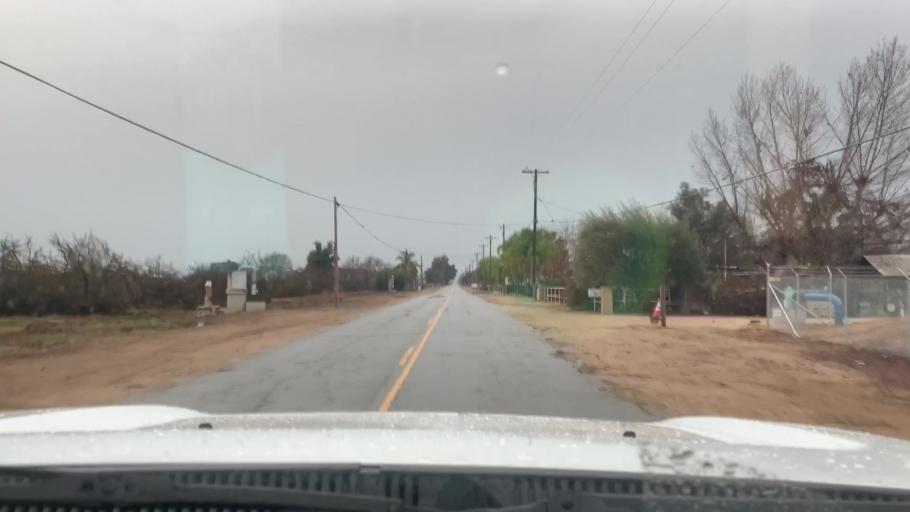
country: US
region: California
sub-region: Kern County
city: Shafter
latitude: 35.4781
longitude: -119.2725
